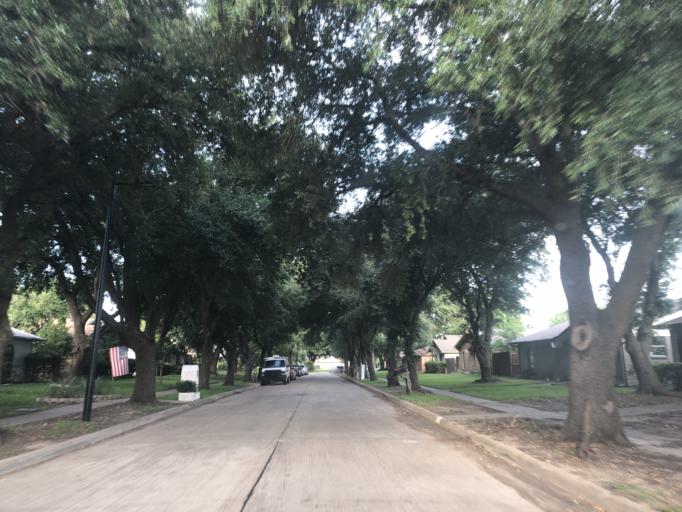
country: US
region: Texas
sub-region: Dallas County
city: Sunnyvale
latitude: 32.8391
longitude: -96.5873
